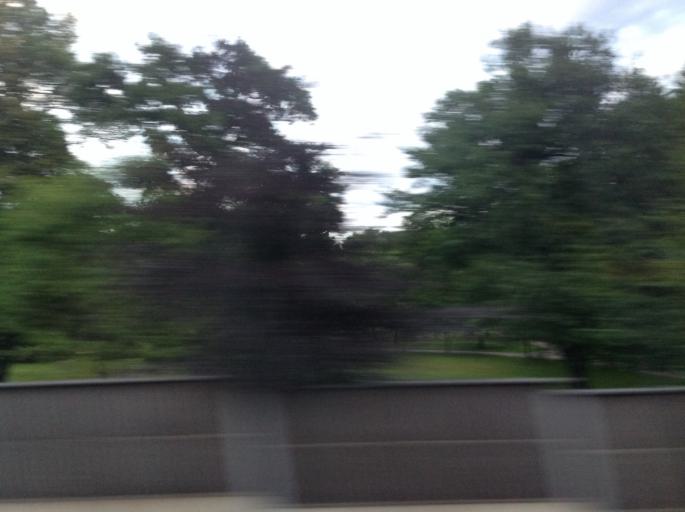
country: AT
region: Salzburg
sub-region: Politischer Bezirk Salzburg-Umgebung
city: Bergheim
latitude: 47.8215
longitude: 13.0535
